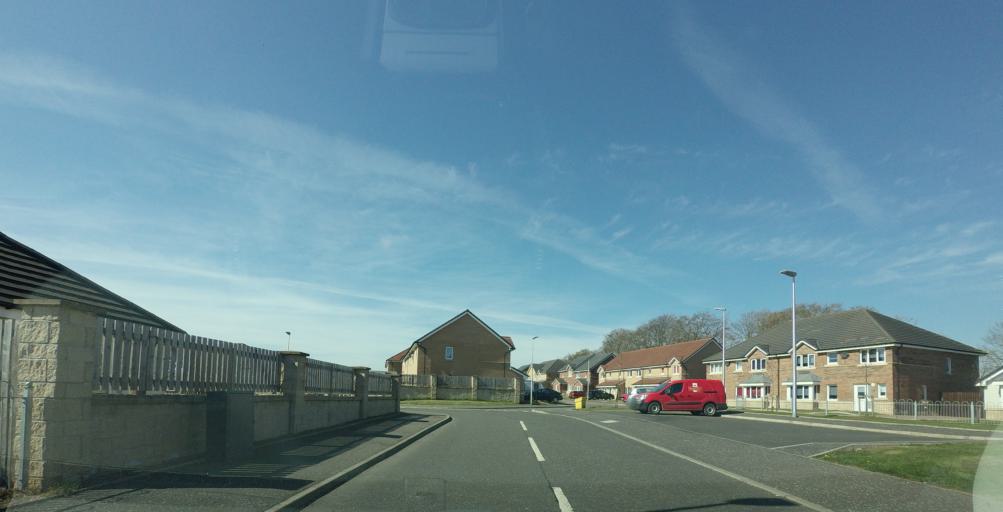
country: GB
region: Scotland
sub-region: West Lothian
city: Blackburn
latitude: 55.8711
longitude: -3.6106
